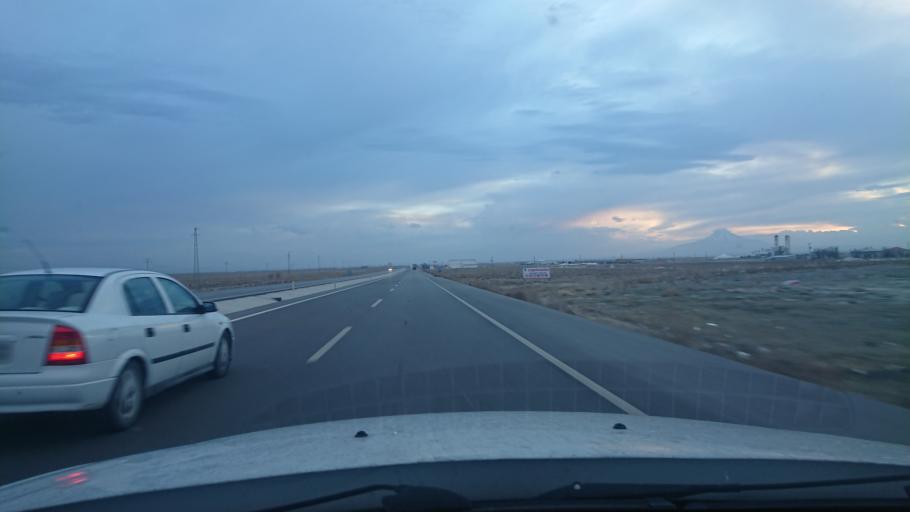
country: TR
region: Aksaray
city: Sultanhani
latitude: 38.2526
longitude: 33.5761
